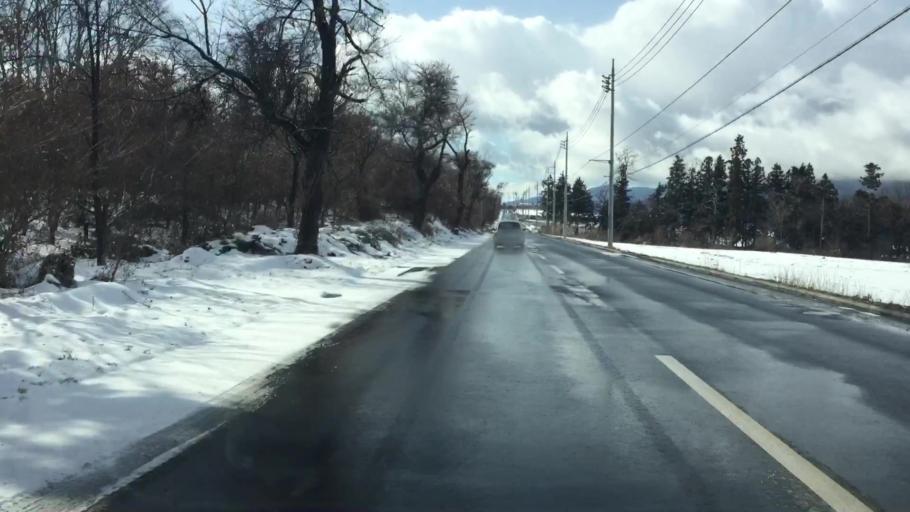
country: JP
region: Gunma
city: Numata
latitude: 36.6190
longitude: 139.0852
